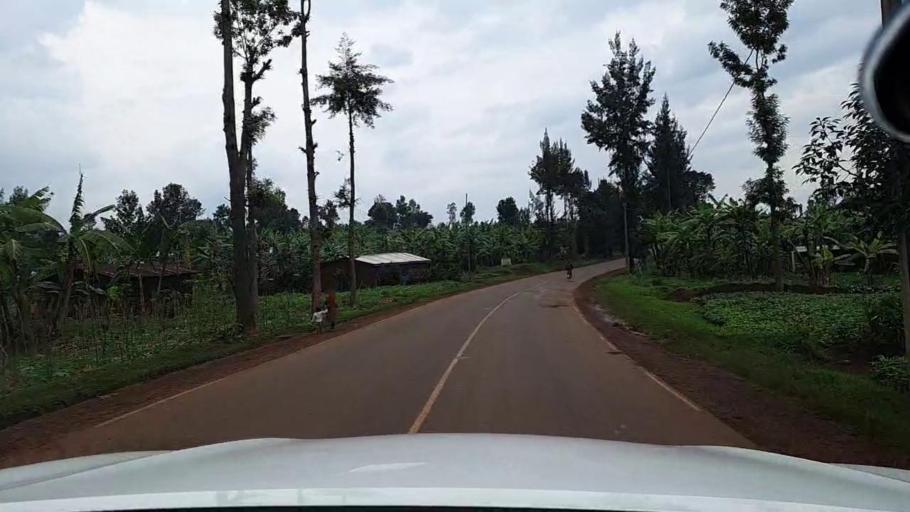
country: RW
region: Western Province
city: Cyangugu
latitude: -2.6150
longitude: 28.9440
